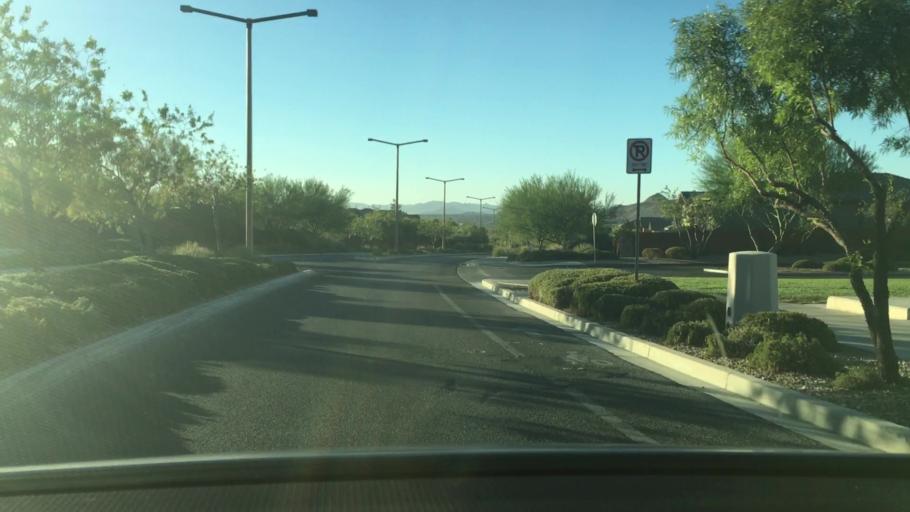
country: US
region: Nevada
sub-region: Clark County
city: Summerlin South
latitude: 36.0901
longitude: -115.3250
